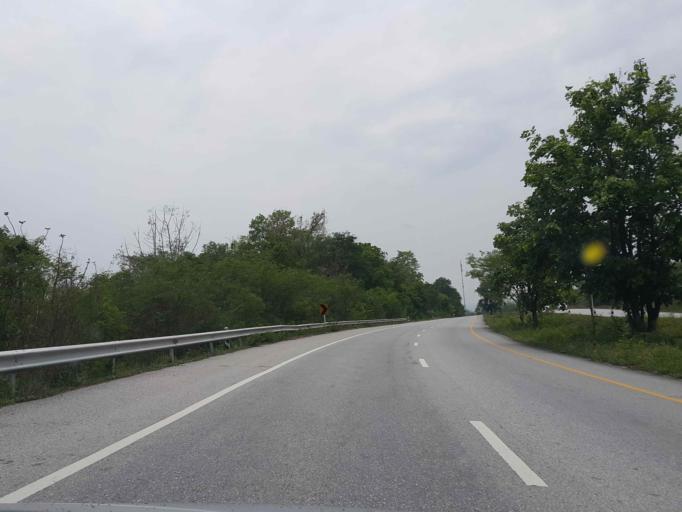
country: TH
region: Lampang
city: Sop Prap
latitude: 17.7680
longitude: 99.2477
